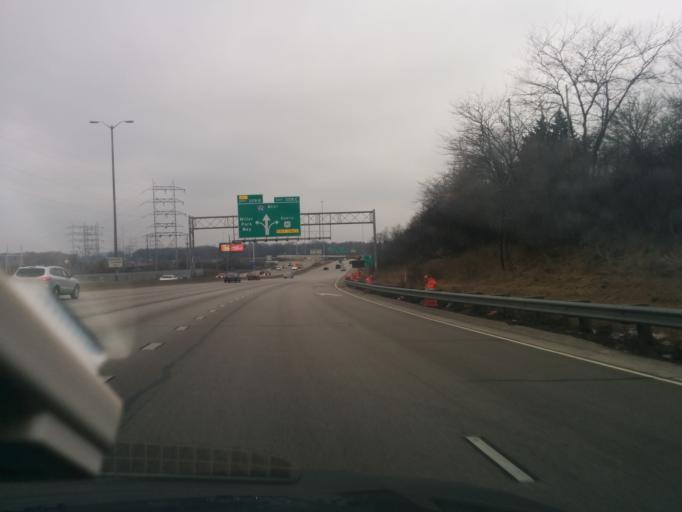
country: US
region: Wisconsin
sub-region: Milwaukee County
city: West Milwaukee
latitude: 43.0324
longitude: -87.9622
